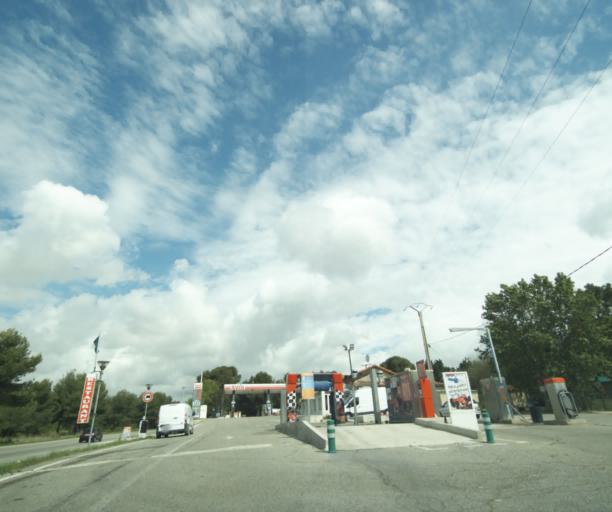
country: FR
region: Provence-Alpes-Cote d'Azur
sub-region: Departement des Bouches-du-Rhone
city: Rognac
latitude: 43.5097
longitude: 5.2059
